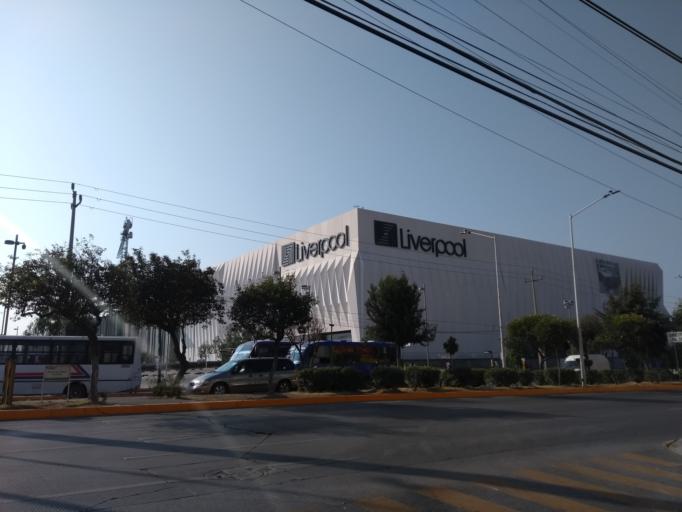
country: MX
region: Puebla
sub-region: Puebla
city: San Sebastian de Aparicio
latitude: 19.0716
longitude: -98.1738
